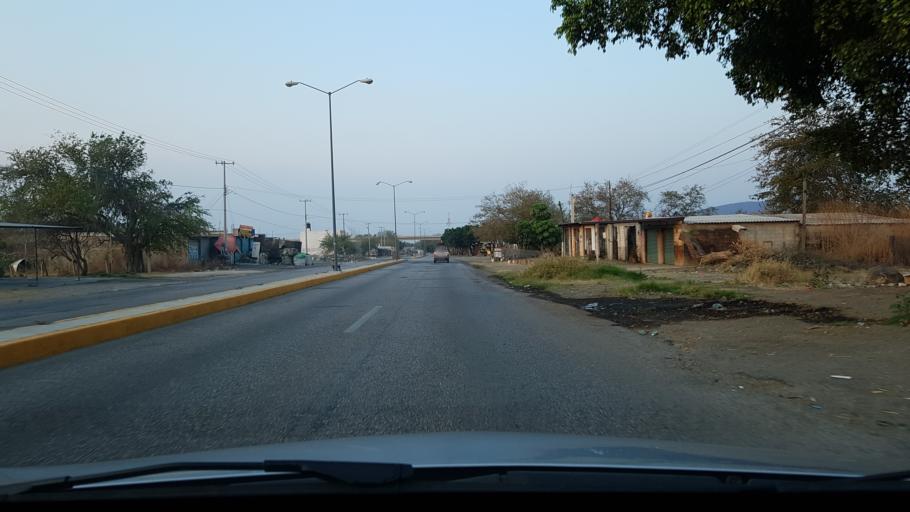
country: MX
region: Morelos
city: Amayuca
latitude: 18.7094
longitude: -98.7988
